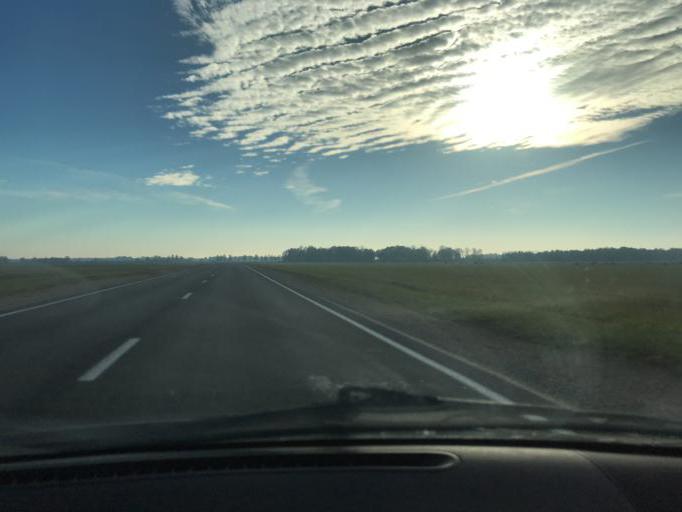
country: BY
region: Brest
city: Drahichyn
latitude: 52.2109
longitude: 25.2021
